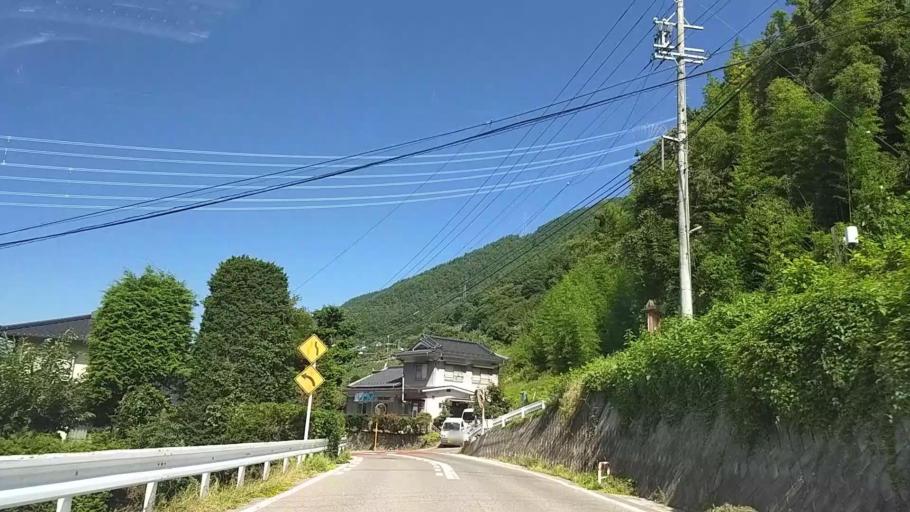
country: JP
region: Nagano
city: Matsumoto
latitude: 36.2224
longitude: 138.0383
